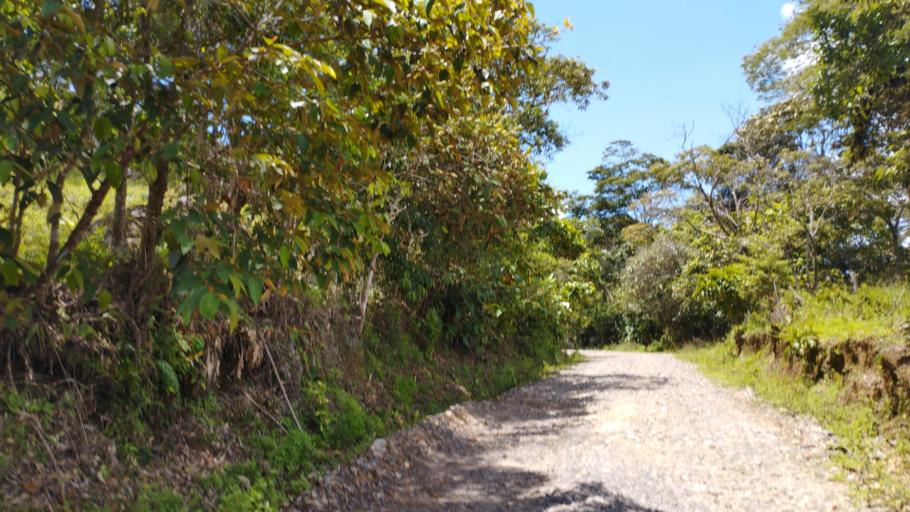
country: CO
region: Boyaca
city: San Luis de Gaceno
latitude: 4.7506
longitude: -73.1397
